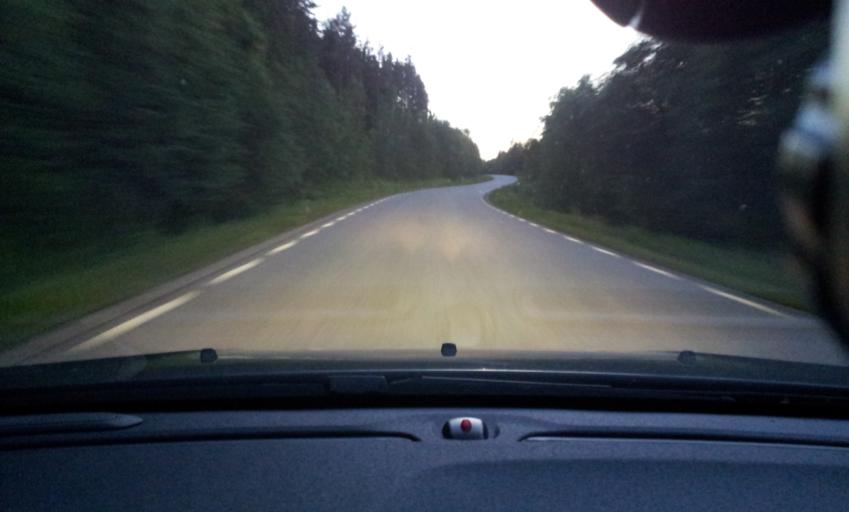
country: SE
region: Jaemtland
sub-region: Braecke Kommun
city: Braecke
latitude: 62.7298
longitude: 15.4052
